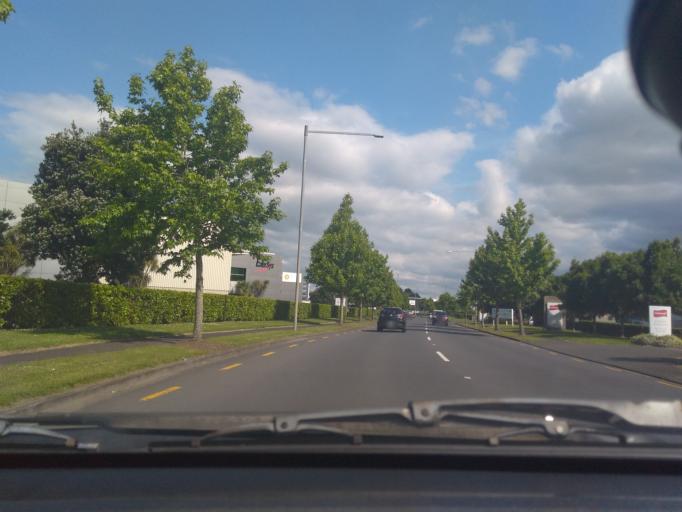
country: NZ
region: Auckland
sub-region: Auckland
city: Tamaki
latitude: -36.9389
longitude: 174.8771
